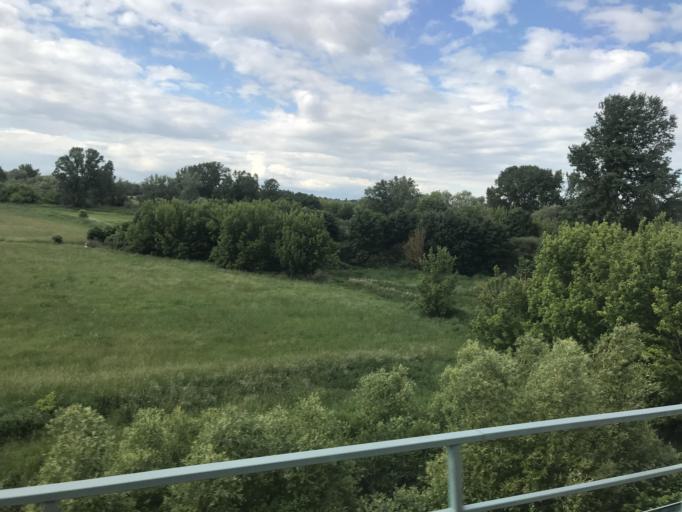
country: DE
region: Saxony-Anhalt
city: Schkopau
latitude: 51.4117
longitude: 11.9768
